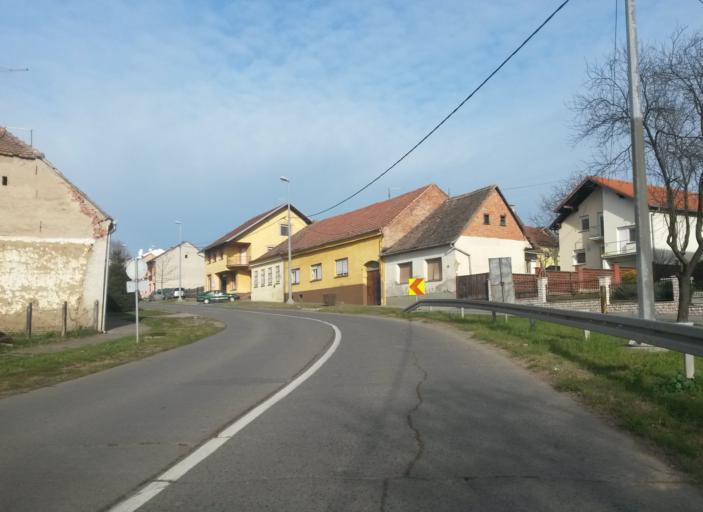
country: HR
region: Osjecko-Baranjska
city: Piskorevci
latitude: 45.3013
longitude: 18.4126
